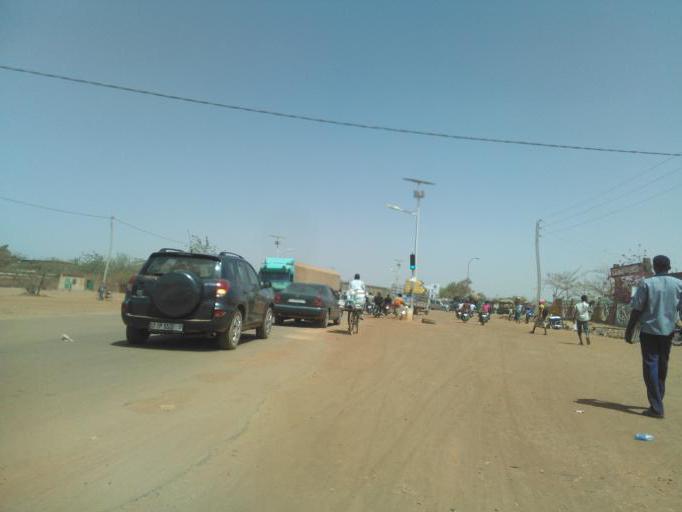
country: BF
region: Centre
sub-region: Kadiogo Province
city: Ouagadougou
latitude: 12.3927
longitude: -1.5675
